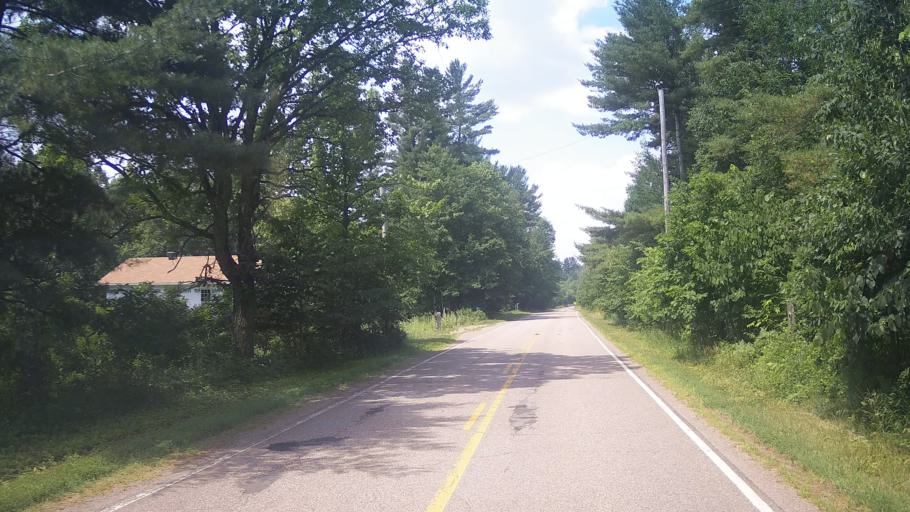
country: CA
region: Quebec
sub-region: Outaouais
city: Shawville
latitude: 45.5229
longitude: -76.4403
